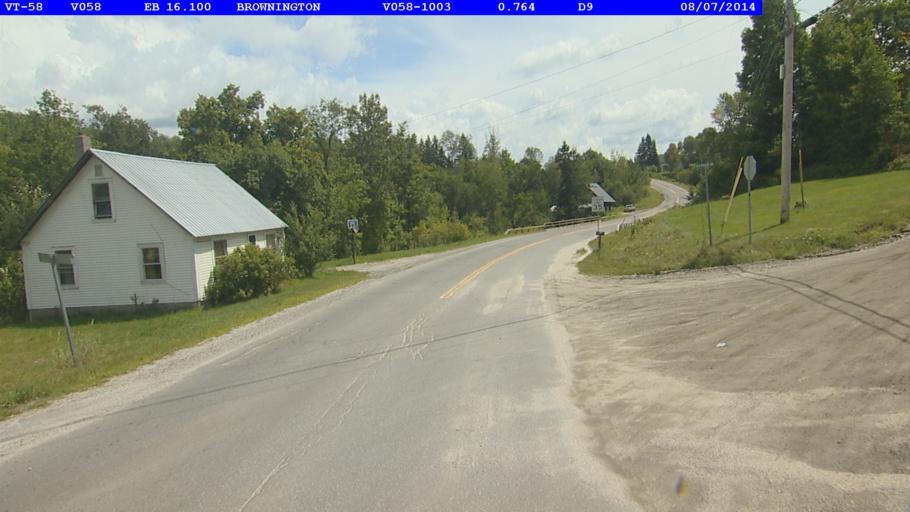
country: US
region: Vermont
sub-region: Orleans County
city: Newport
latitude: 44.8029
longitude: -72.1303
